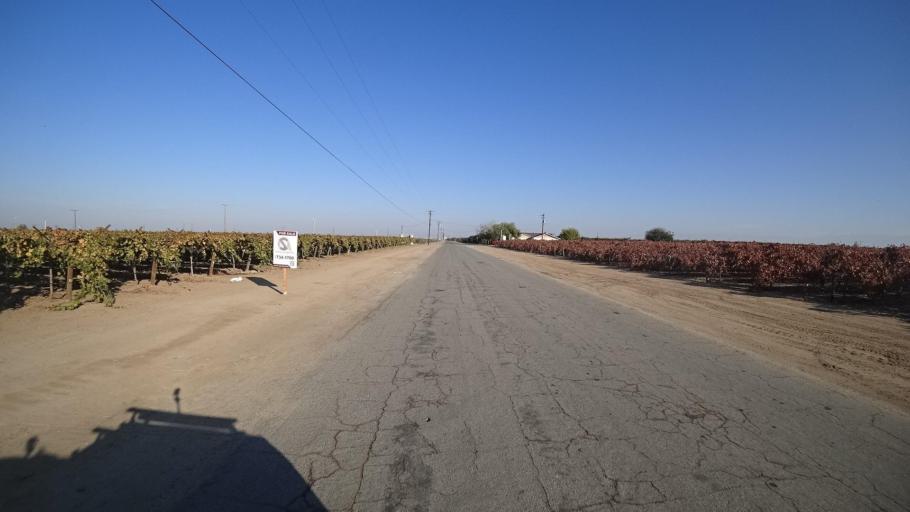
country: US
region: California
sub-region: Tulare County
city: Richgrove
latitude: 35.7714
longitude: -119.1518
